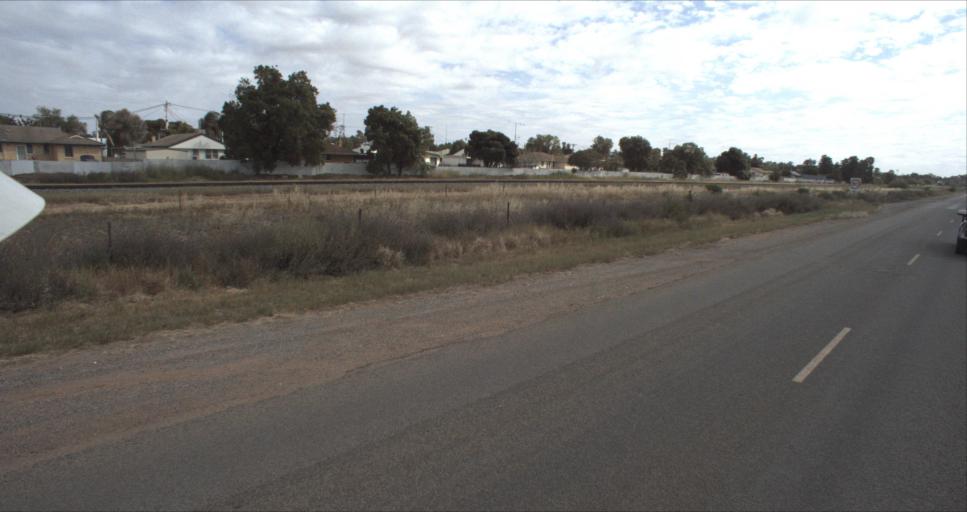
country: AU
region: New South Wales
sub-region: Leeton
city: Leeton
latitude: -34.5677
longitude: 146.3957
